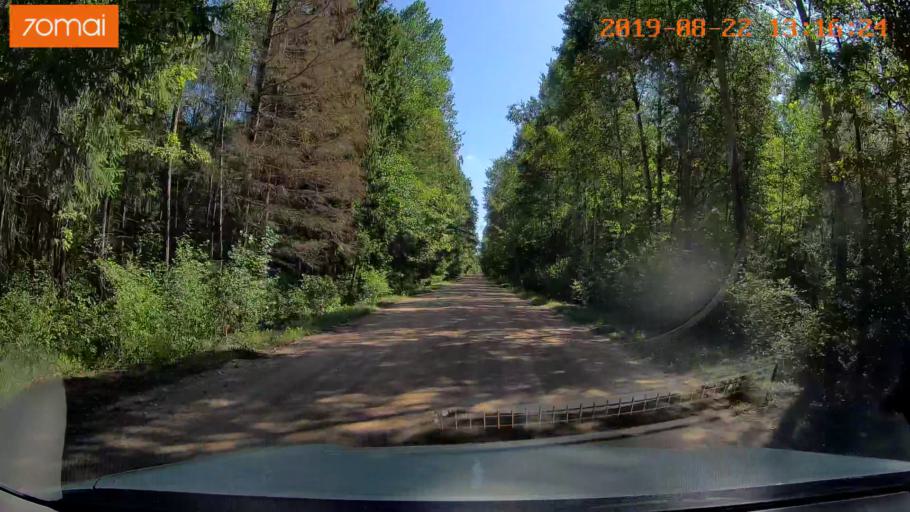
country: BY
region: Minsk
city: Prawdzinski
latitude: 53.2560
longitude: 27.9106
